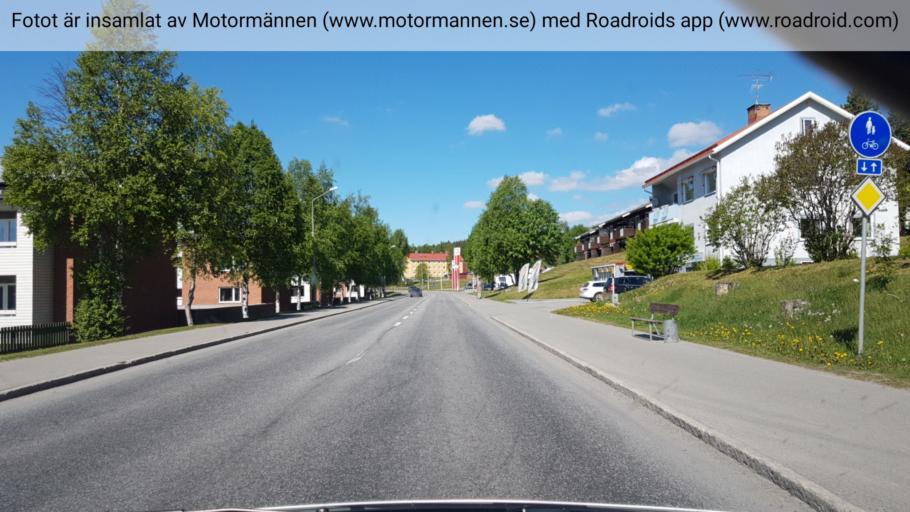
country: SE
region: Vaesterbotten
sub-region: Vilhelmina Kommun
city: Vilhelmina
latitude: 64.6227
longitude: 16.6645
